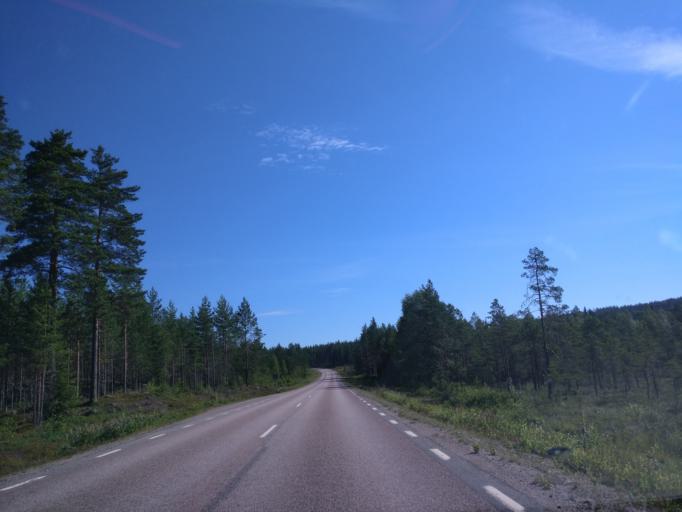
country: SE
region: Vaermland
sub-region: Hagfors Kommun
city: Hagfors
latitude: 60.0277
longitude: 13.9099
